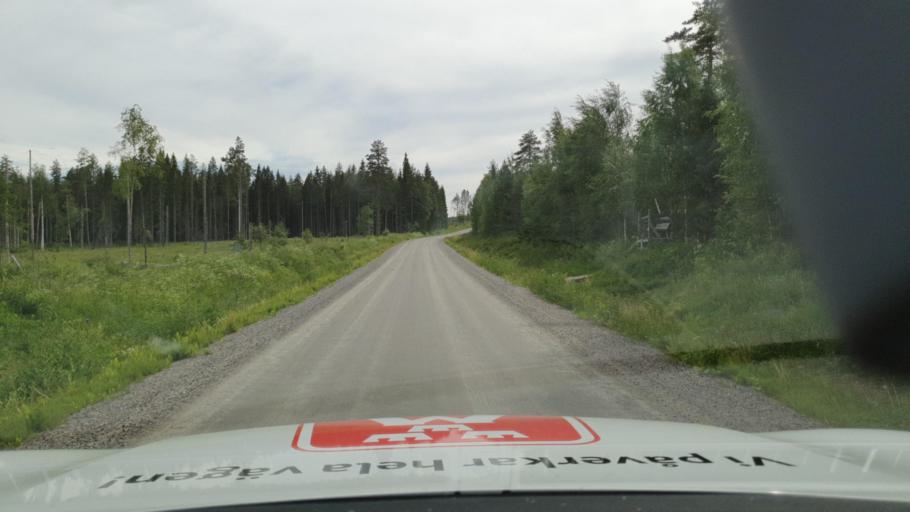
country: SE
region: Vaesterbotten
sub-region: Skelleftea Kommun
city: Burea
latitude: 64.4213
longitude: 21.0098
